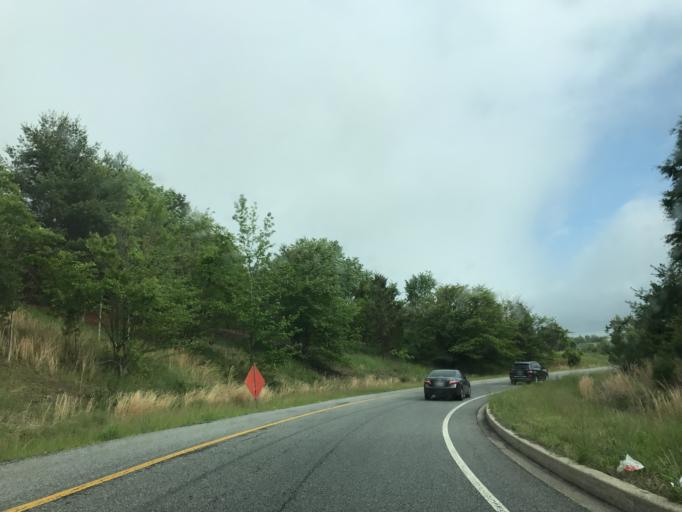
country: US
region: Maryland
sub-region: Prince George's County
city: Bowie
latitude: 38.9543
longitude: -76.7416
